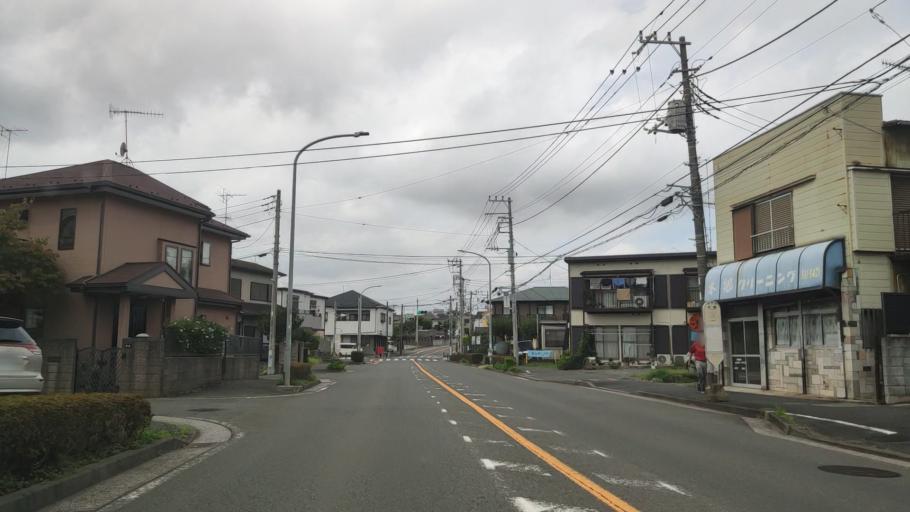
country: JP
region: Kanagawa
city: Minami-rinkan
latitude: 35.4741
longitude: 139.4772
